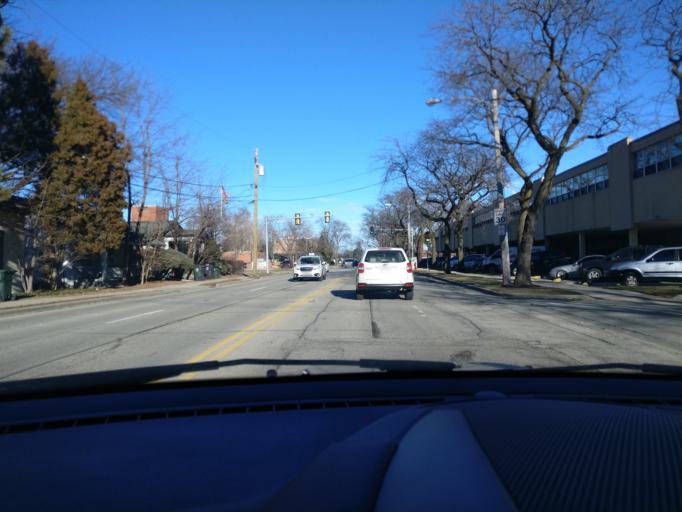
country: US
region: Illinois
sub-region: Cook County
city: Skokie
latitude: 42.0446
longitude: -87.7532
